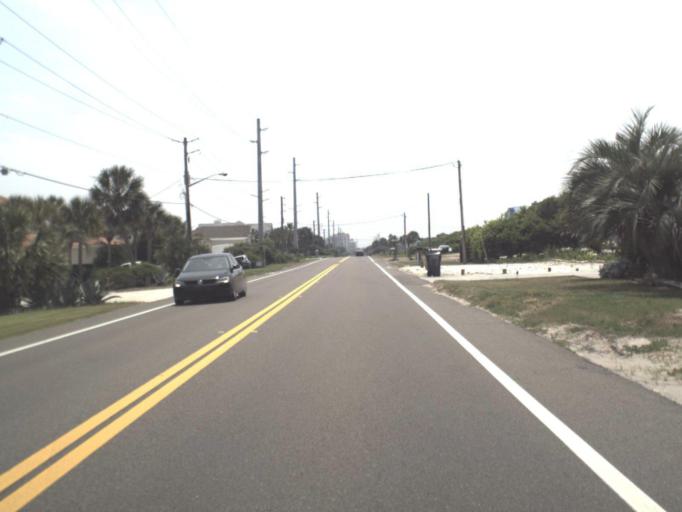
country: US
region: Florida
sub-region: Nassau County
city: Fernandina Beach
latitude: 30.6127
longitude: -81.4422
